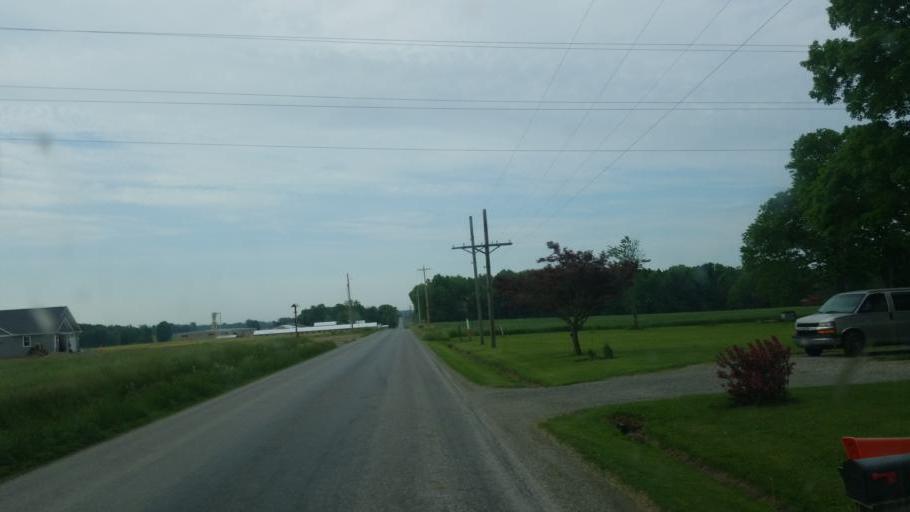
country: US
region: Ohio
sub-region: Wayne County
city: Dalton
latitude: 40.7710
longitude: -81.7551
